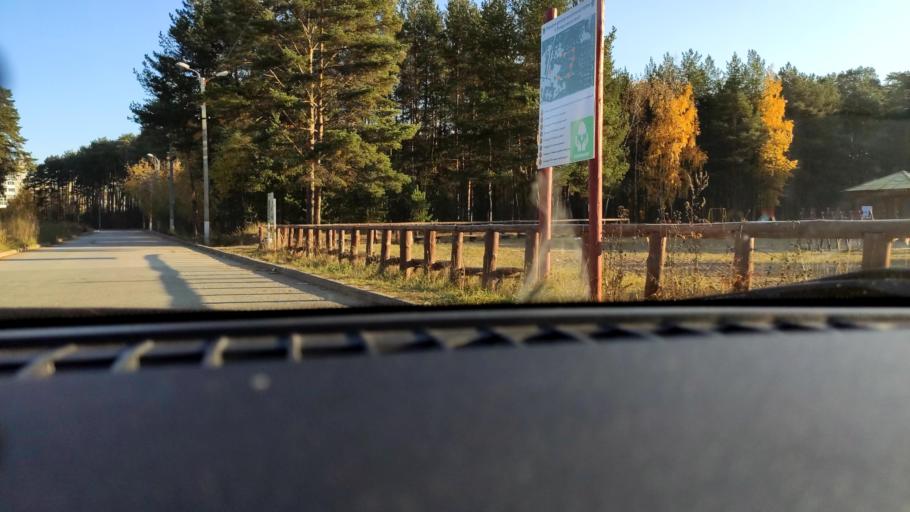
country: RU
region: Perm
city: Kondratovo
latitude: 57.9901
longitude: 56.1422
